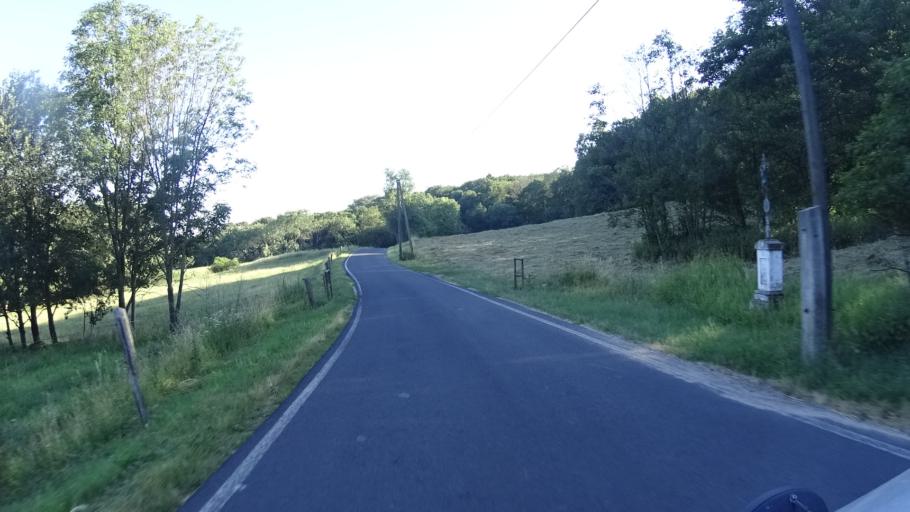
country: CZ
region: Ustecky
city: Zitenice
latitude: 50.5776
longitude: 14.1269
